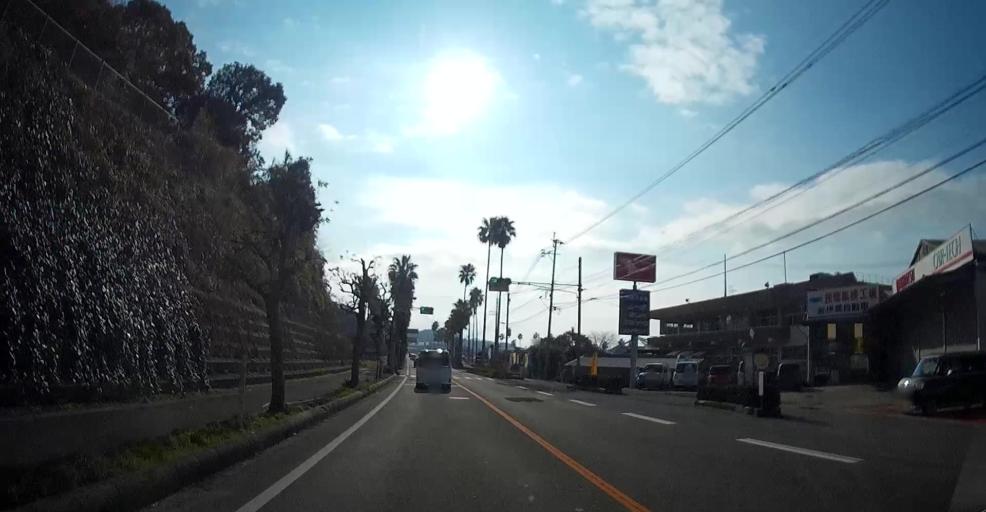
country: JP
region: Kumamoto
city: Yatsushiro
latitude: 32.5782
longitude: 130.4220
